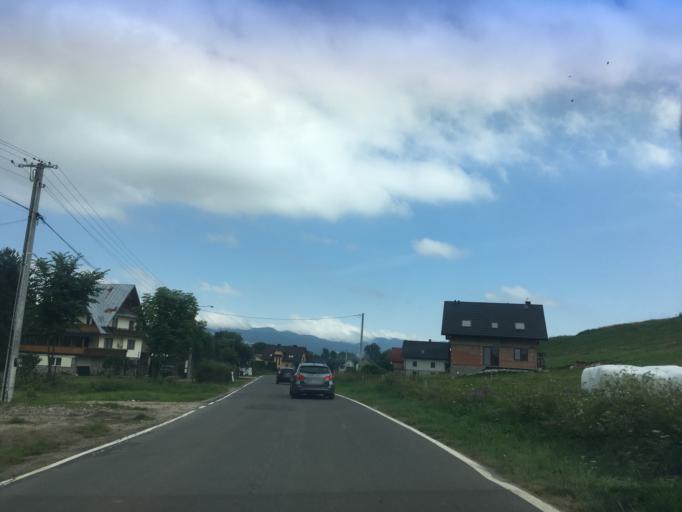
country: PL
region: Lesser Poland Voivodeship
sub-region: Powiat nowotarski
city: Frydman
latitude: 49.4372
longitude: 20.1750
